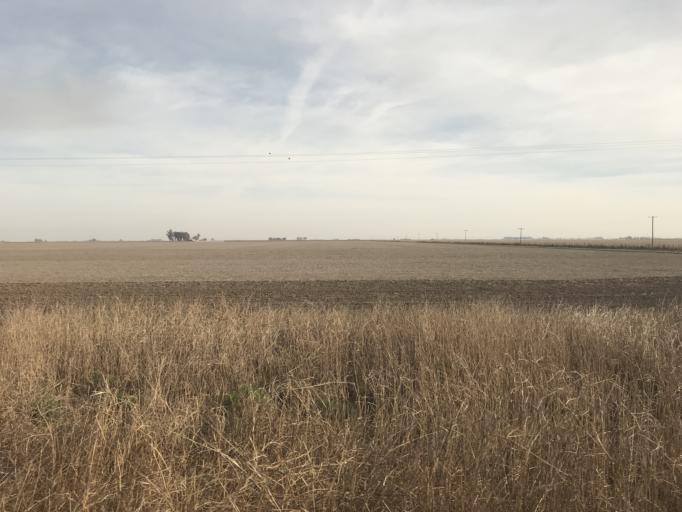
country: AR
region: Cordoba
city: Pilar
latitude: -31.7288
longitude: -63.8450
